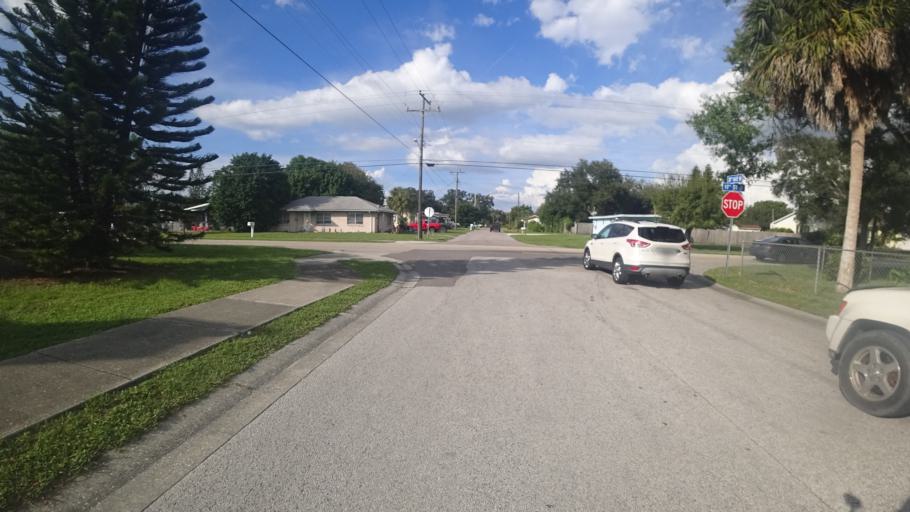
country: US
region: Florida
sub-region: Manatee County
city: Palmetto
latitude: 27.5212
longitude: -82.5893
